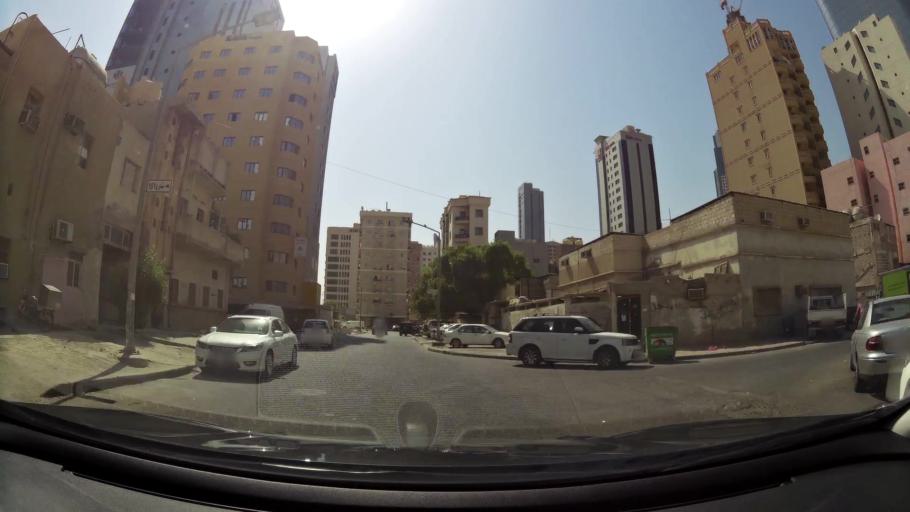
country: KW
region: Al Asimah
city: Ad Dasmah
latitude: 29.3795
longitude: 47.9952
